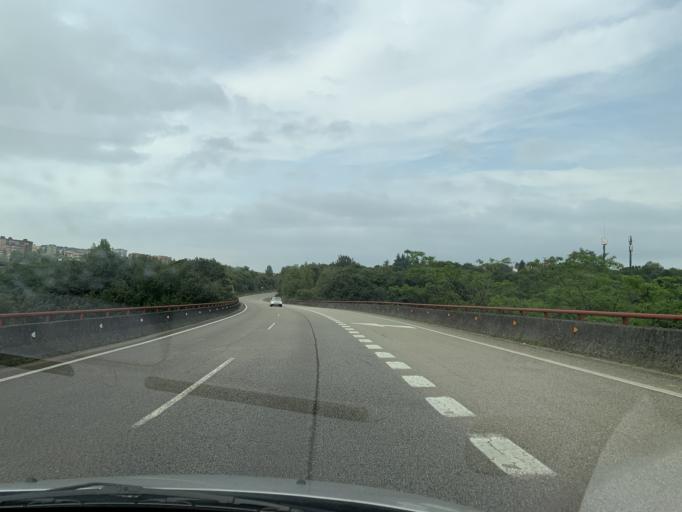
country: ES
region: Asturias
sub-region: Province of Asturias
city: Oviedo
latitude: 43.3457
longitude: -5.8588
